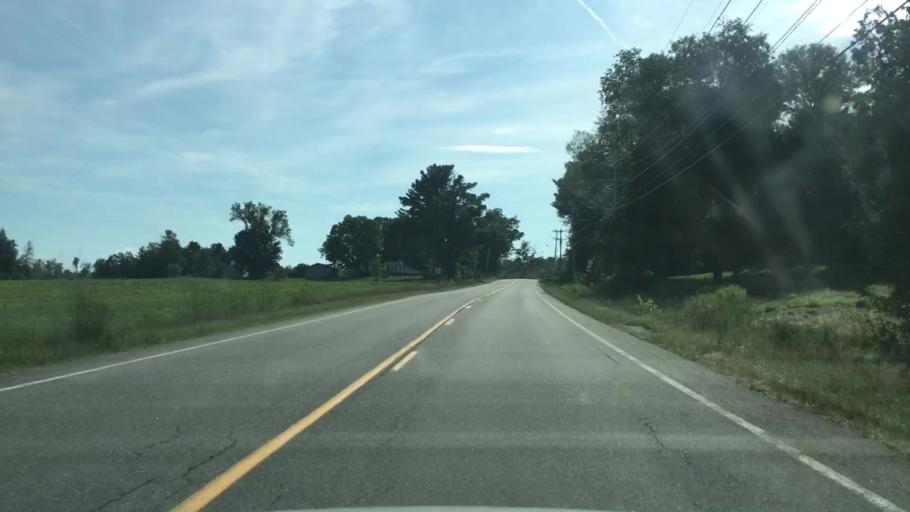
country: US
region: Maine
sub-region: Penobscot County
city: Lincoln
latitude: 45.4079
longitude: -68.5005
